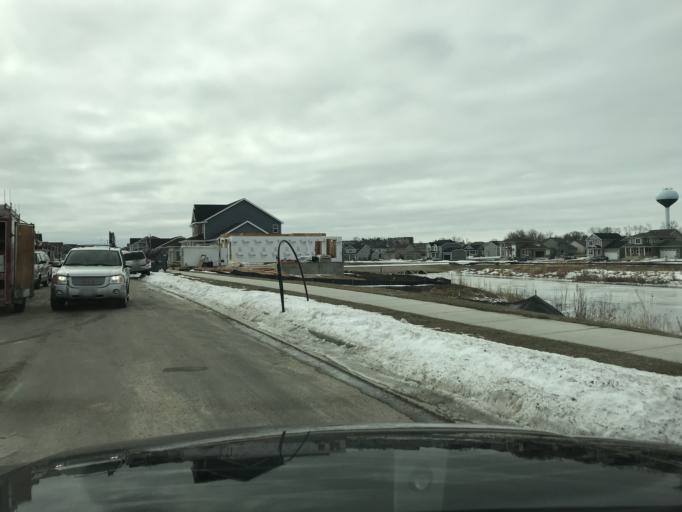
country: US
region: Wisconsin
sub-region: Dane County
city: Monona
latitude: 43.0957
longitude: -89.2724
